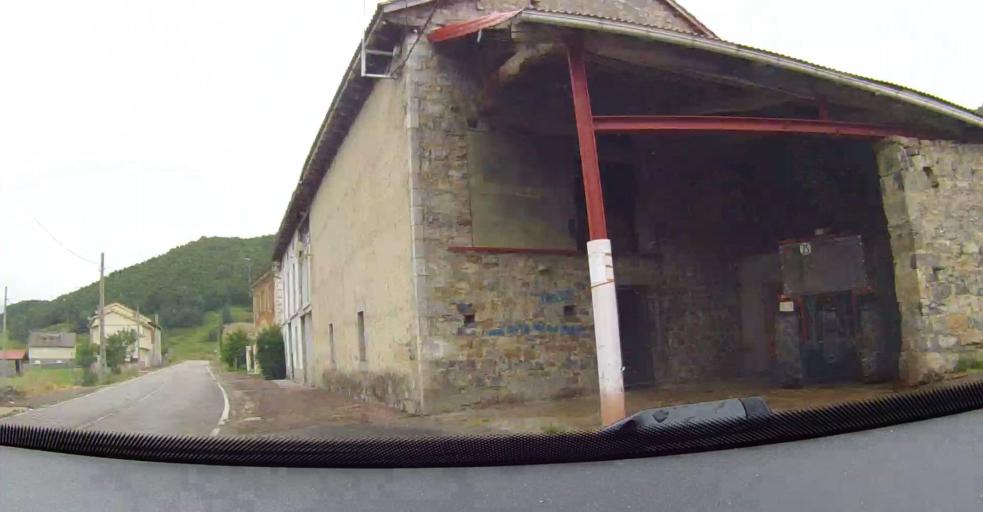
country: ES
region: Castille and Leon
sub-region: Provincia de Leon
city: Acebedo
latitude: 43.0632
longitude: -5.1380
